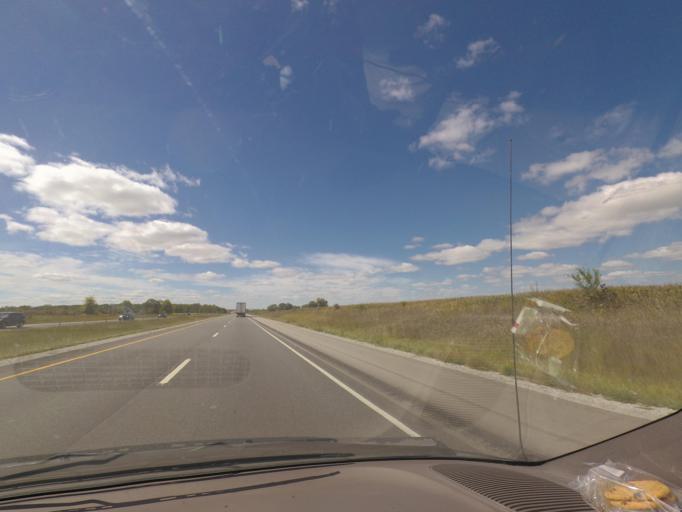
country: US
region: Indiana
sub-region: Henry County
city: Knightstown
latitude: 39.8304
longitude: -85.5886
